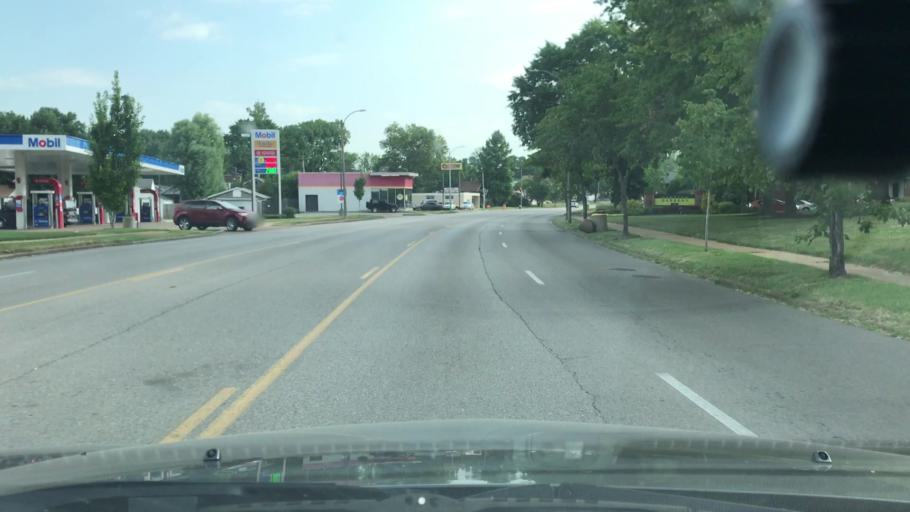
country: US
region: Missouri
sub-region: Saint Louis County
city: Maplewood
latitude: 38.6032
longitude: -90.2916
